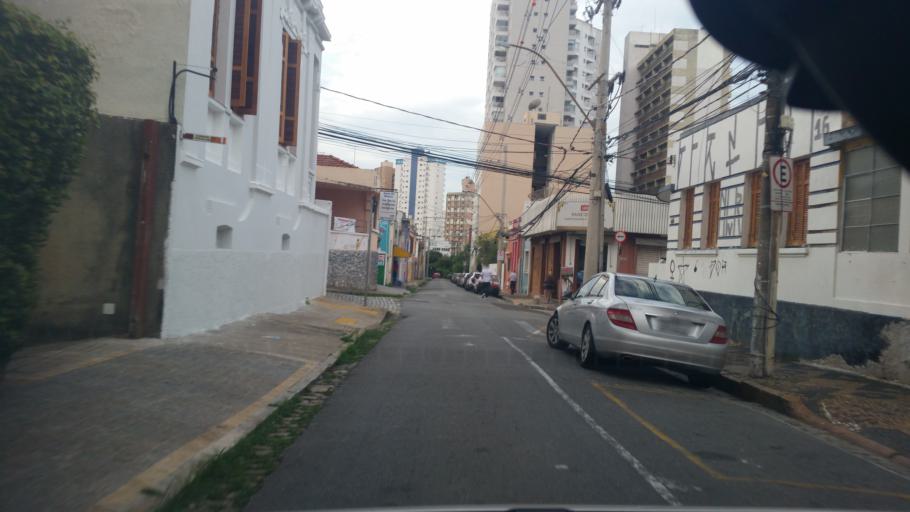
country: BR
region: Sao Paulo
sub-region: Campinas
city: Campinas
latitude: -22.8994
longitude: -47.0592
